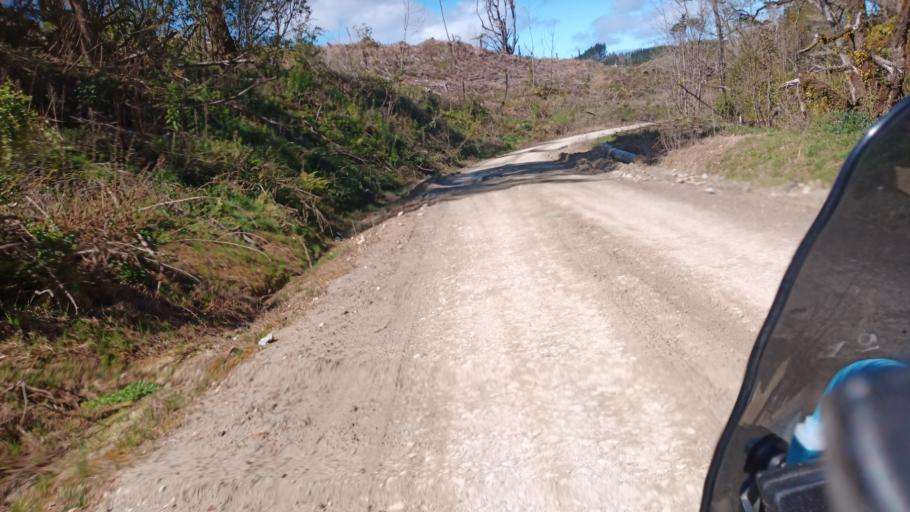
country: NZ
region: Gisborne
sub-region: Gisborne District
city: Gisborne
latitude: -38.8897
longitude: 177.7908
